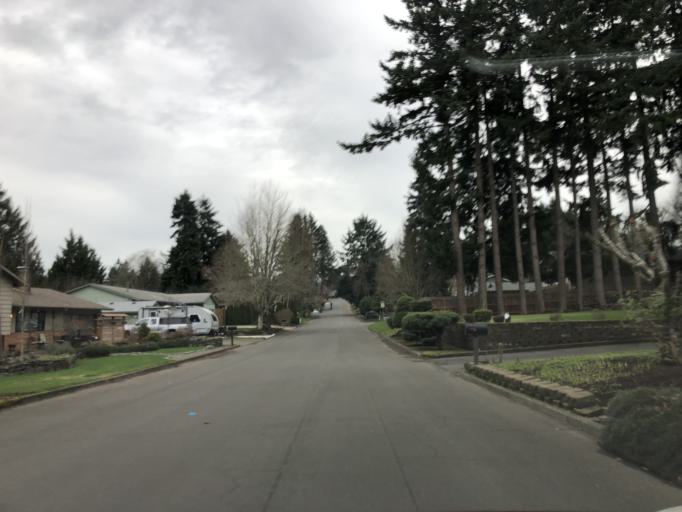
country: US
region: Oregon
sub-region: Washington County
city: King City
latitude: 45.4250
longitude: -122.7967
